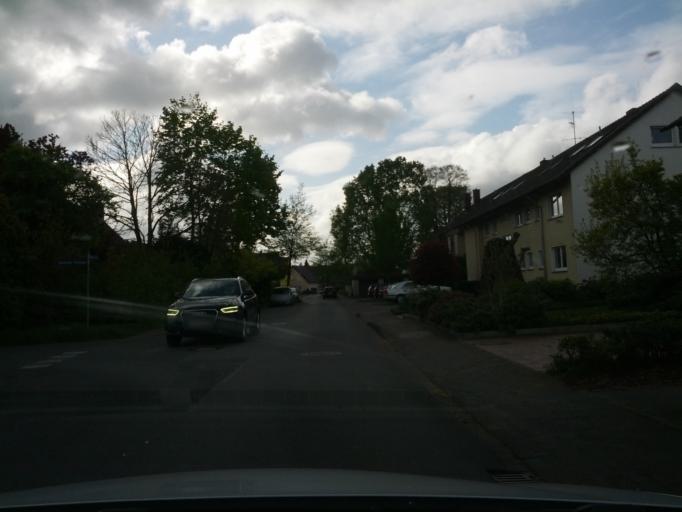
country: DE
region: North Rhine-Westphalia
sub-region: Regierungsbezirk Detmold
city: Guetersloh
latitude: 51.8803
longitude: 8.3866
